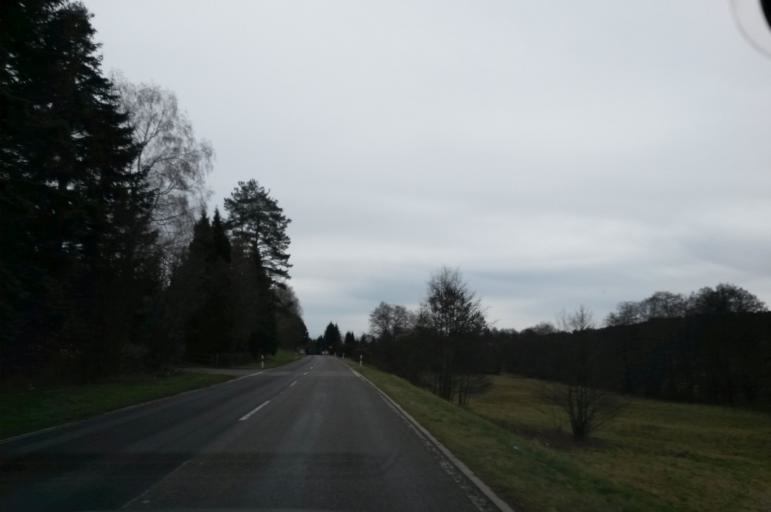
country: DE
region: Baden-Wuerttemberg
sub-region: Karlsruhe Region
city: Dobel
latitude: 48.8421
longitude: 8.4884
